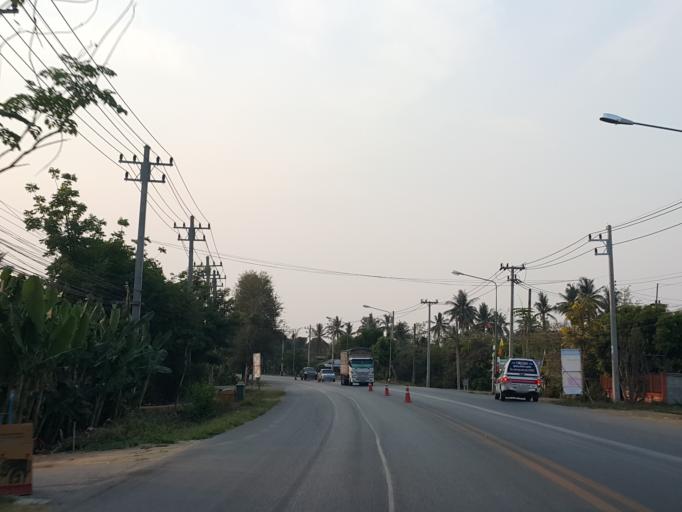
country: TH
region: Sukhothai
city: Sawankhalok
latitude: 17.2508
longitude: 99.8583
